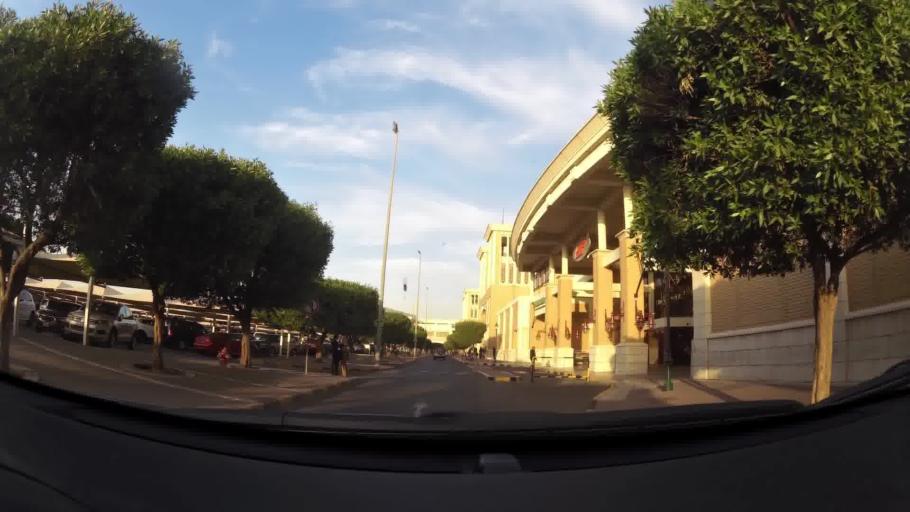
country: KW
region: Al Asimah
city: Kuwait City
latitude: 29.3885
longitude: 47.9798
